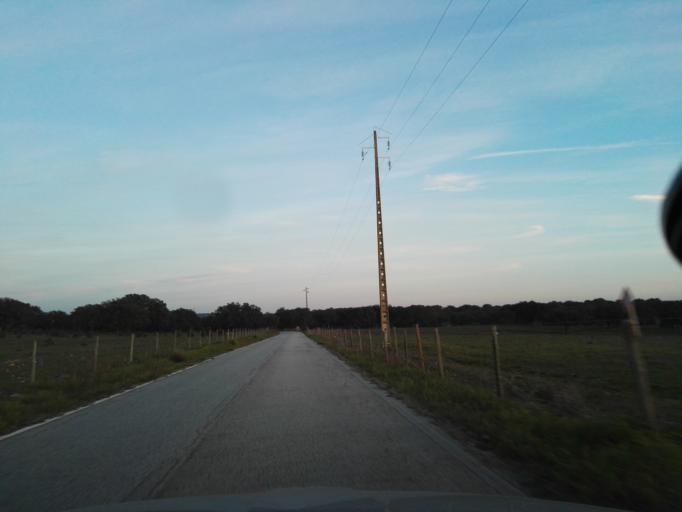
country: PT
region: Evora
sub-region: Montemor-O-Novo
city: Montemor-o-Novo
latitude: 38.7597
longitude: -8.1726
